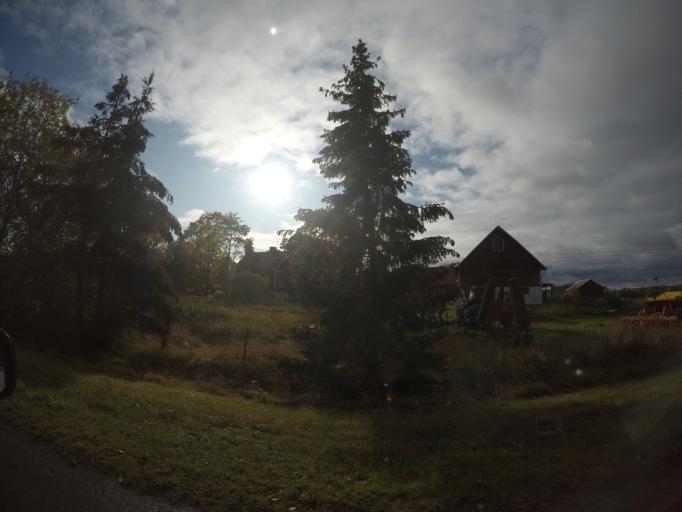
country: SE
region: Soedermanland
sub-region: Eskilstuna Kommun
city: Kvicksund
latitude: 59.3159
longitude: 16.2715
